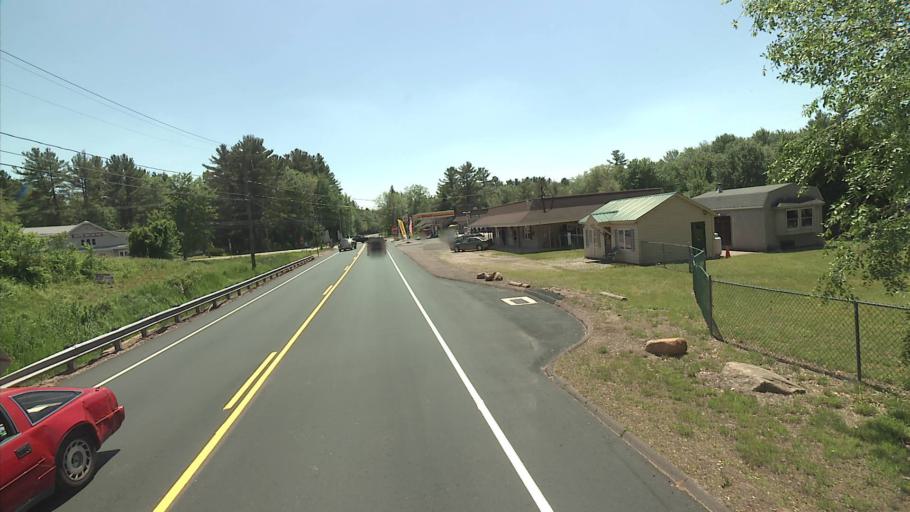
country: US
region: Connecticut
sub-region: Tolland County
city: Crystal Lake
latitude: 41.9307
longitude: -72.3829
